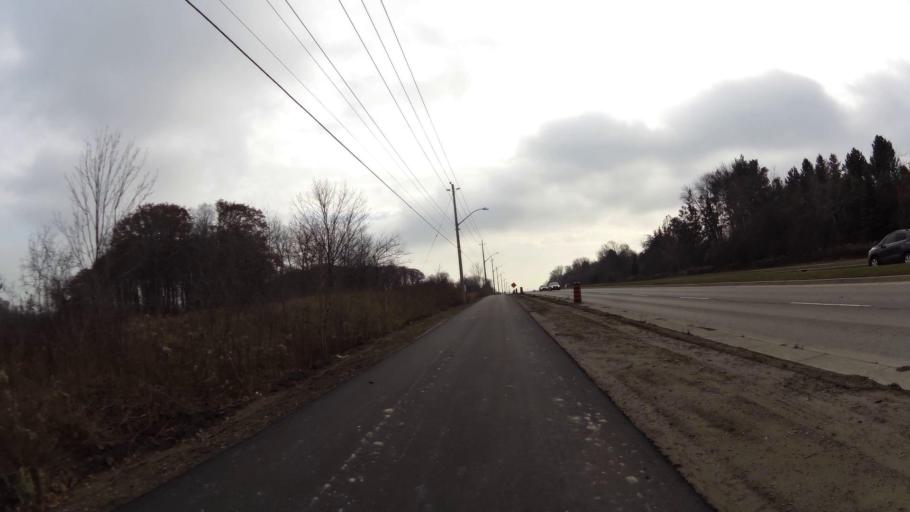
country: CA
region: Ontario
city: Kitchener
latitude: 43.4133
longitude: -80.4646
